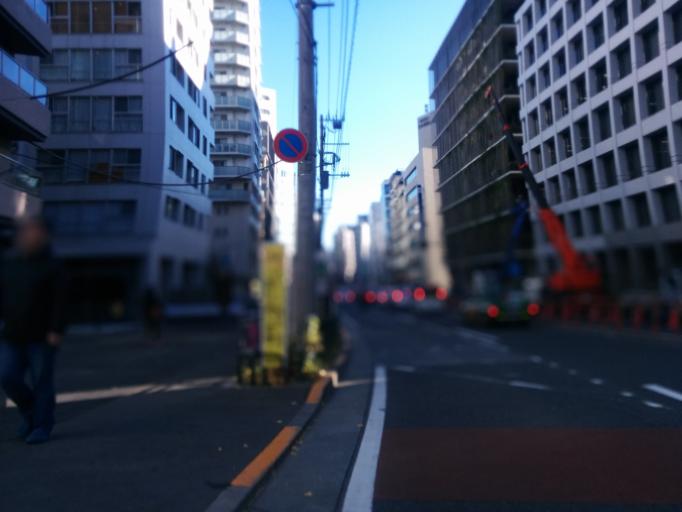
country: JP
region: Tokyo
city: Tokyo
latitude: 35.6796
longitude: 139.7047
